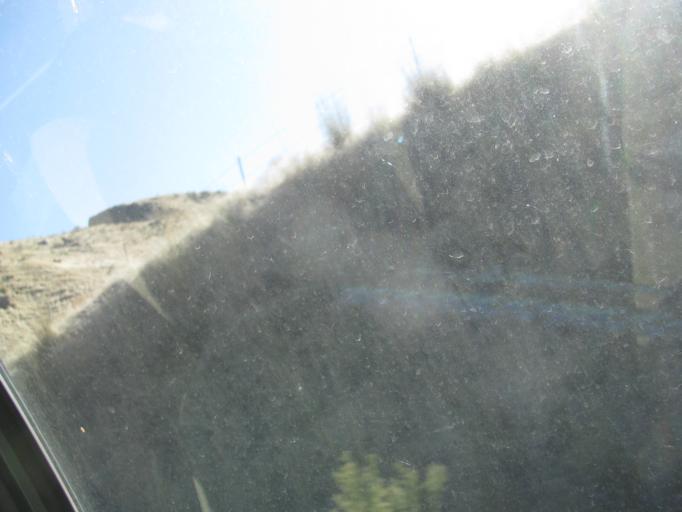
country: US
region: Washington
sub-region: Asotin County
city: Asotin
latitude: 46.3179
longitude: -117.0499
